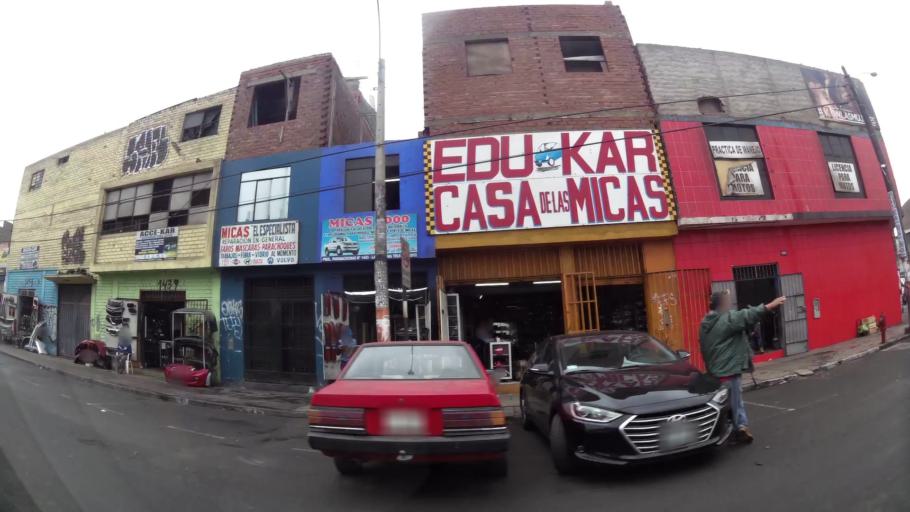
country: PE
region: Lima
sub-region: Lima
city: San Luis
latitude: -12.0728
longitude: -77.0163
